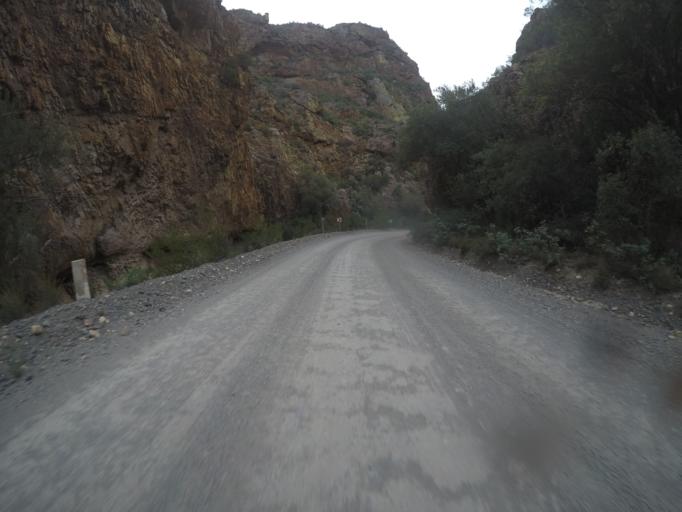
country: ZA
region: Eastern Cape
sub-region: Cacadu District Municipality
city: Willowmore
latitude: -33.5212
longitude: 23.6512
